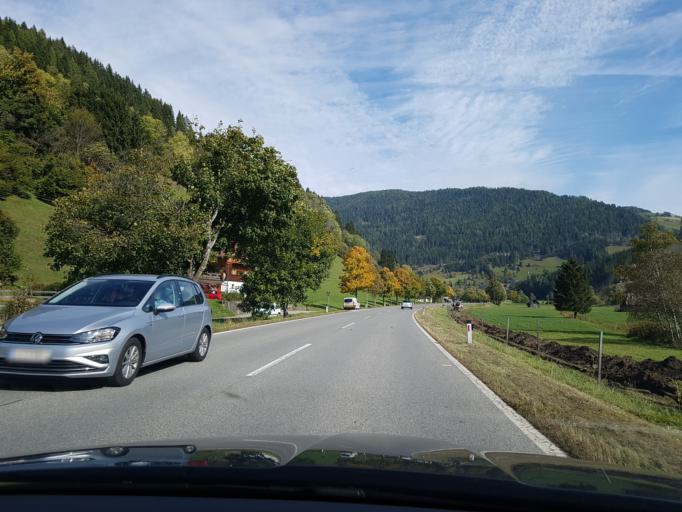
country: AT
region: Carinthia
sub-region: Politischer Bezirk Spittal an der Drau
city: Kleinkirchheim
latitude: 46.8460
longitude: 13.8826
